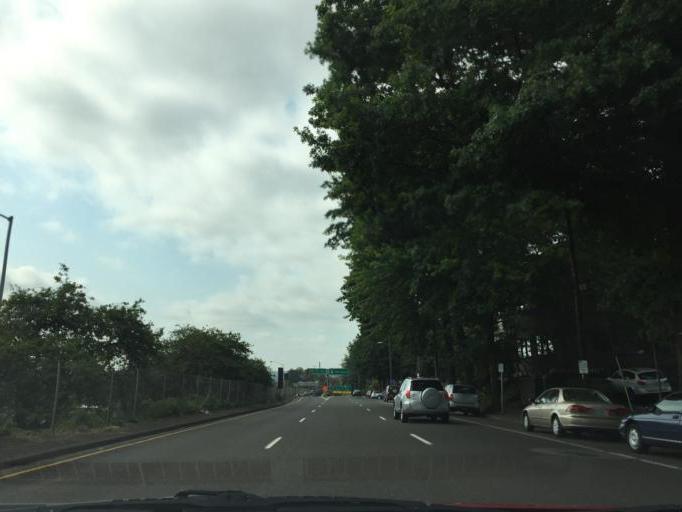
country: US
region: Oregon
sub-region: Multnomah County
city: Portland
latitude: 45.4974
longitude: -122.6738
